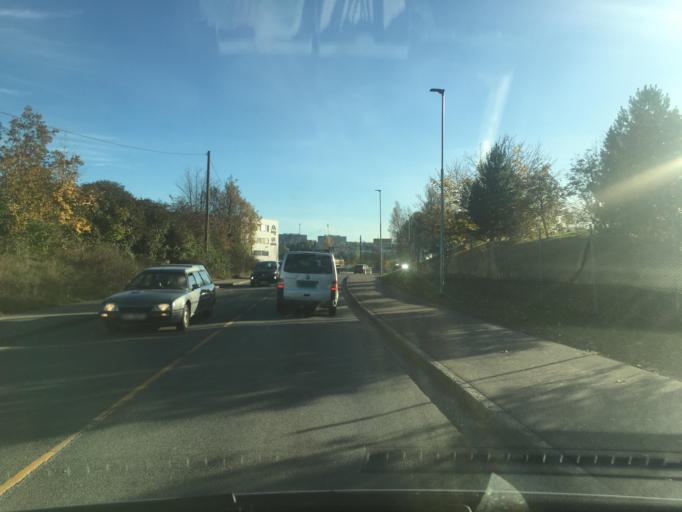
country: NO
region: Oslo
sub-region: Oslo
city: Oslo
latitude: 59.9313
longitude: 10.8301
